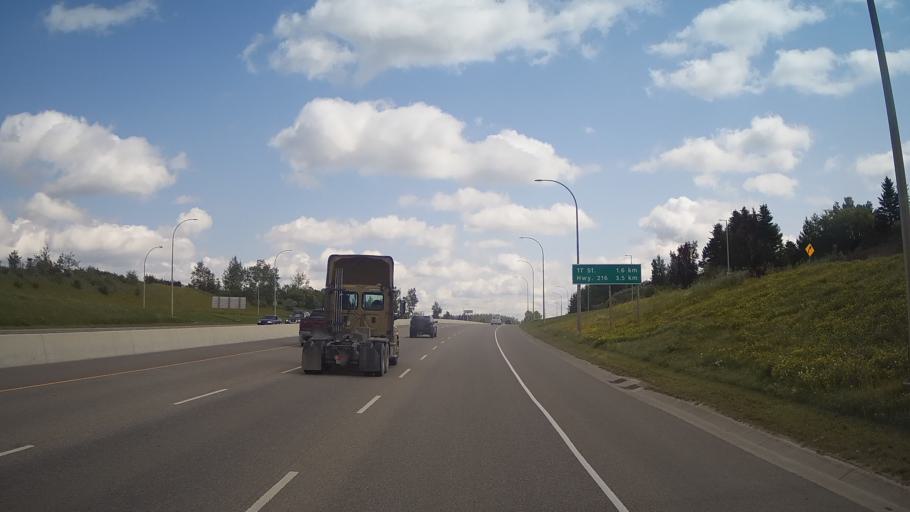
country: CA
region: Alberta
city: Sherwood Park
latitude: 53.4868
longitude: -113.3921
